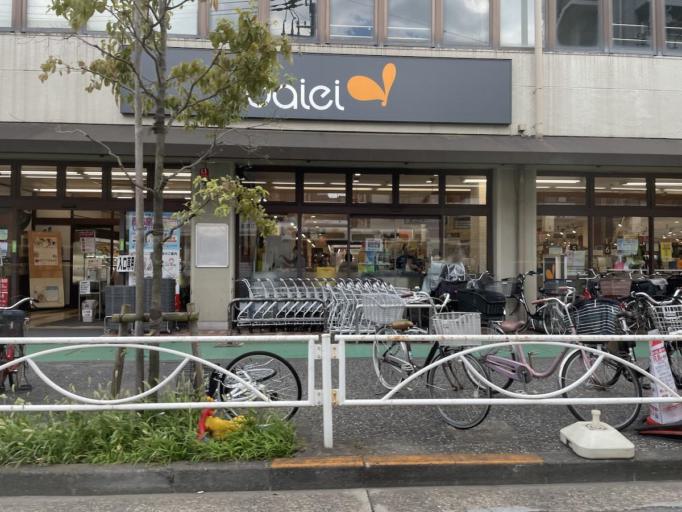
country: JP
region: Tokyo
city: Urayasu
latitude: 35.7069
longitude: 139.8305
